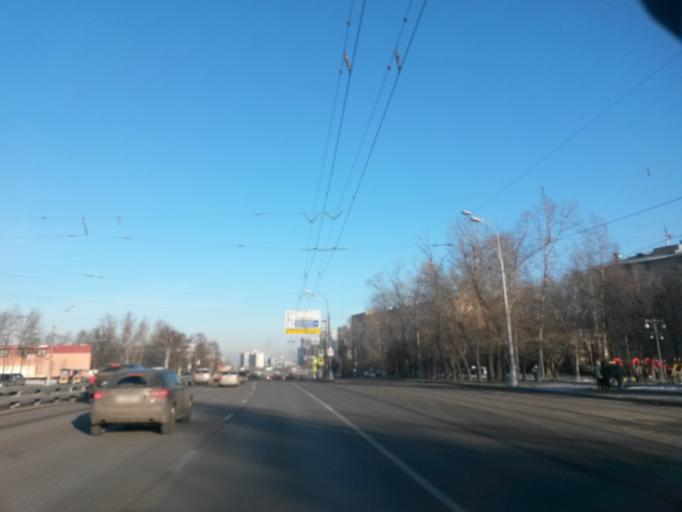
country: RU
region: Moscow
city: Nagornyy
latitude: 55.6678
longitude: 37.6239
